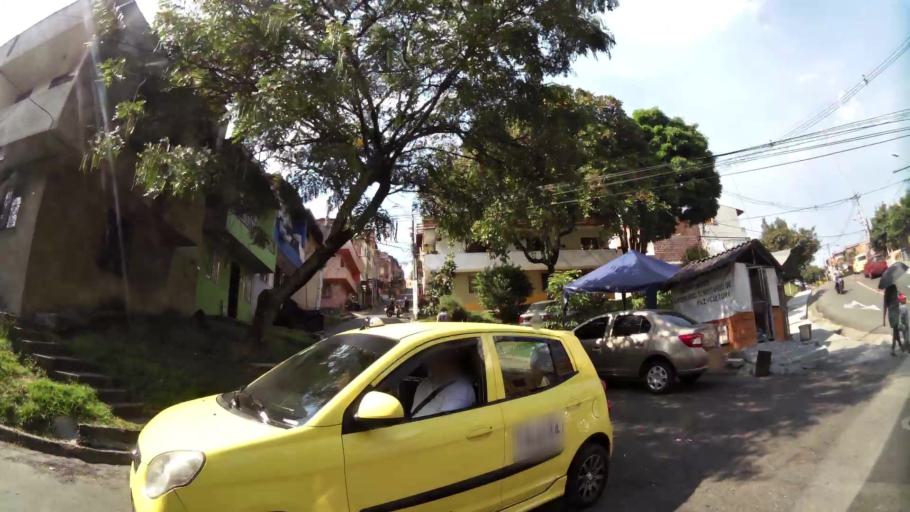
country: CO
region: Antioquia
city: Medellin
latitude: 6.2839
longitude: -75.5931
